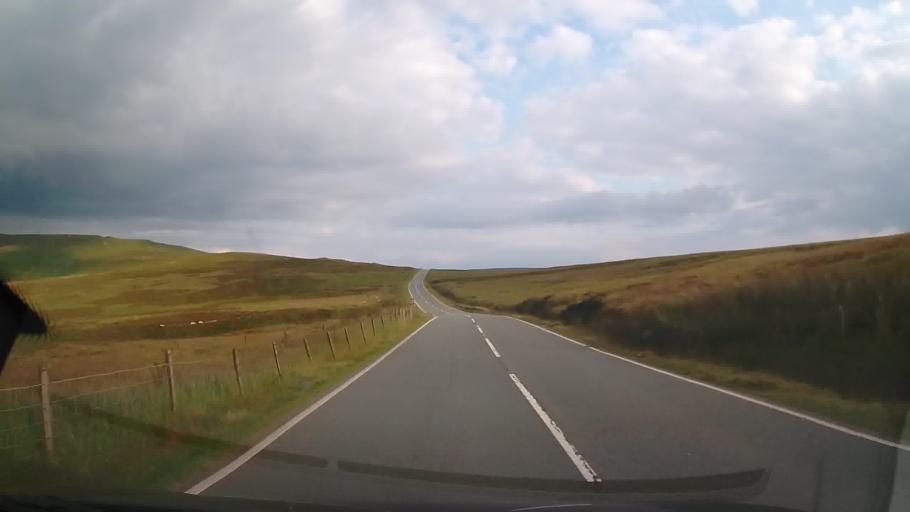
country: GB
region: Wales
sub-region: Denbighshire
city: Llandrillo
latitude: 52.8682
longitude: -3.4657
